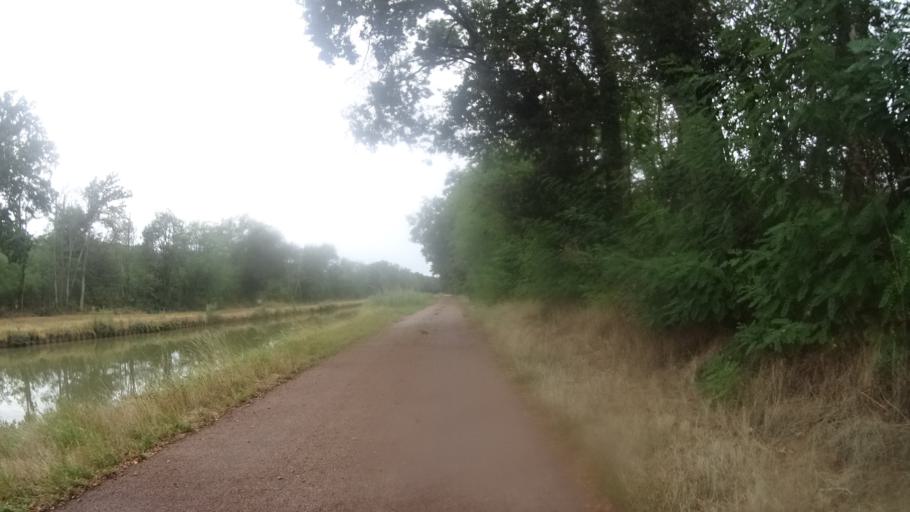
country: FR
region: Bourgogne
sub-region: Departement de la Nievre
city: Imphy
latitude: 46.8762
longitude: 3.2660
